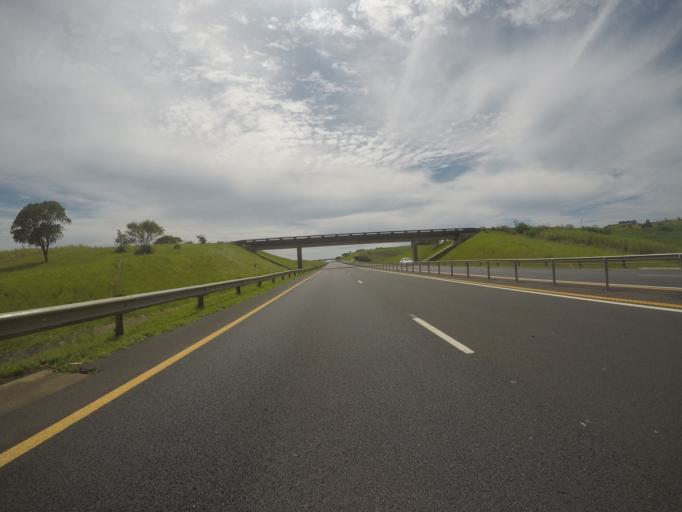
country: ZA
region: KwaZulu-Natal
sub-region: iLembe District Municipality
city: Mandeni
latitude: -29.1787
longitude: 31.5011
